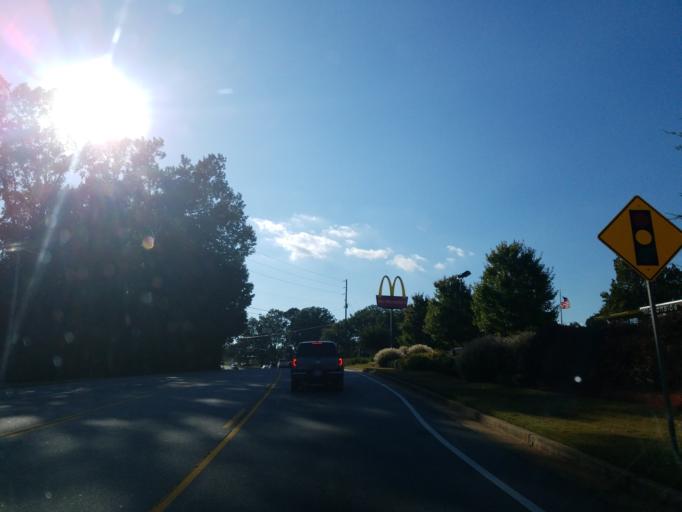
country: US
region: Georgia
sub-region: Paulding County
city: Dallas
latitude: 33.9108
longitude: -84.8016
